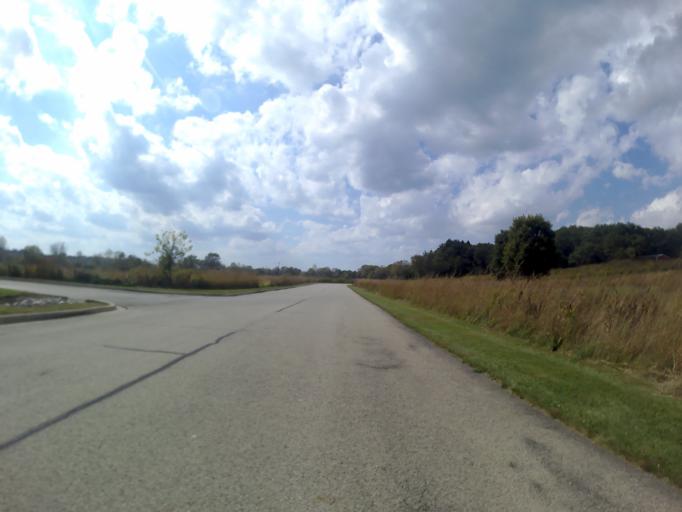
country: US
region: Illinois
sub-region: Will County
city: Bolingbrook
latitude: 41.7164
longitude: -88.1019
